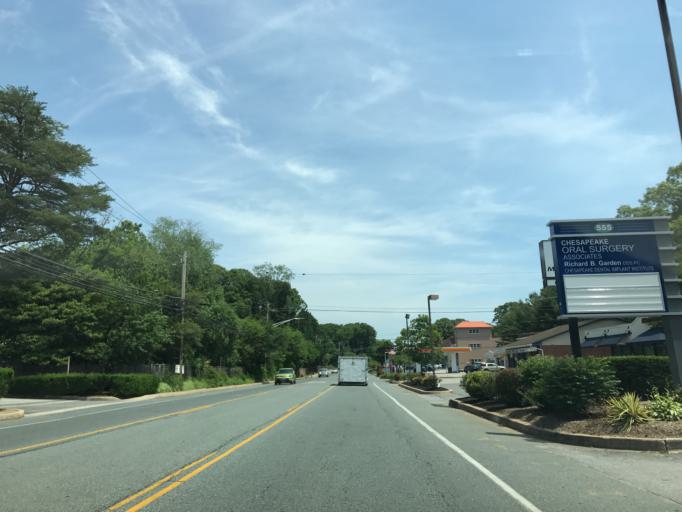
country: US
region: Maryland
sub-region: Anne Arundel County
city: Arden on the Severn
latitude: 39.0819
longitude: -76.5831
